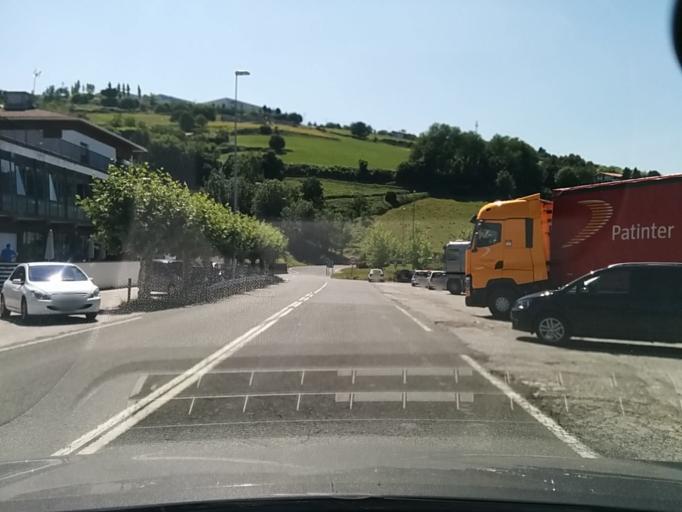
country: ES
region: Basque Country
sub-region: Provincia de Guipuzcoa
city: Deba
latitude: 43.2787
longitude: -2.3306
